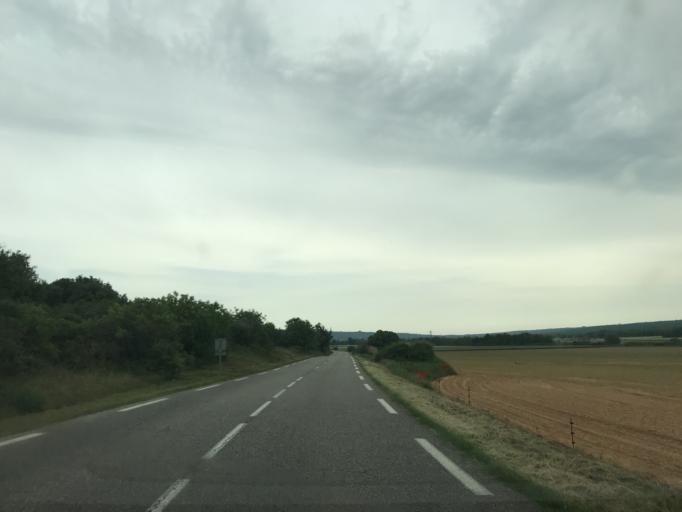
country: FR
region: Provence-Alpes-Cote d'Azur
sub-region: Departement du Var
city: Ginasservis
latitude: 43.6426
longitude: 5.8074
